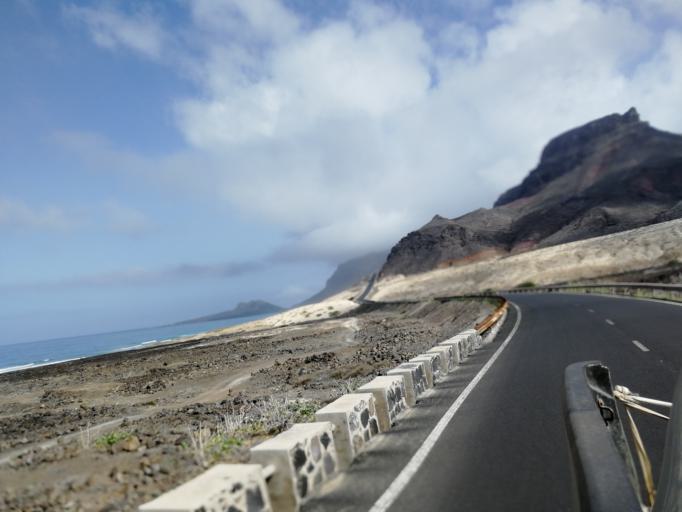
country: CV
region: Sao Vicente
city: Mindelo
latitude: 16.8739
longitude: -24.9089
